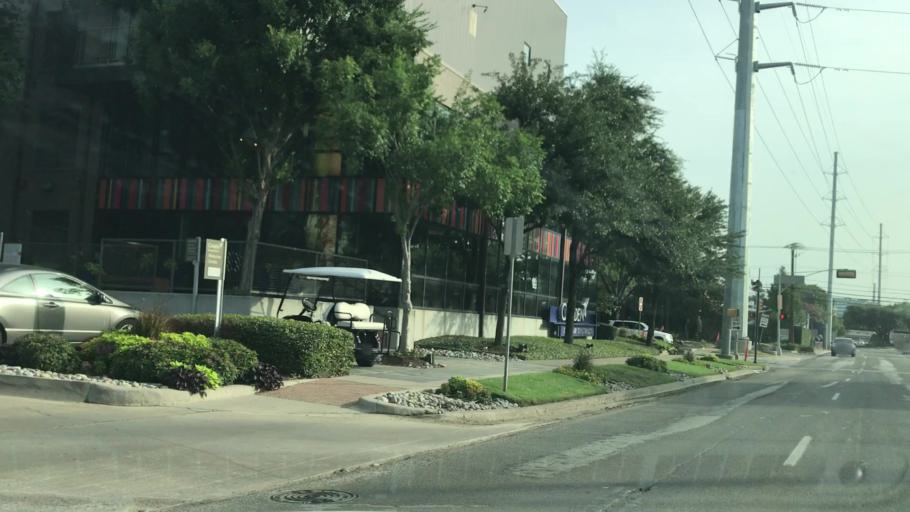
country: US
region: Texas
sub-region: Dallas County
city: Dallas
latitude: 32.7960
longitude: -96.8205
